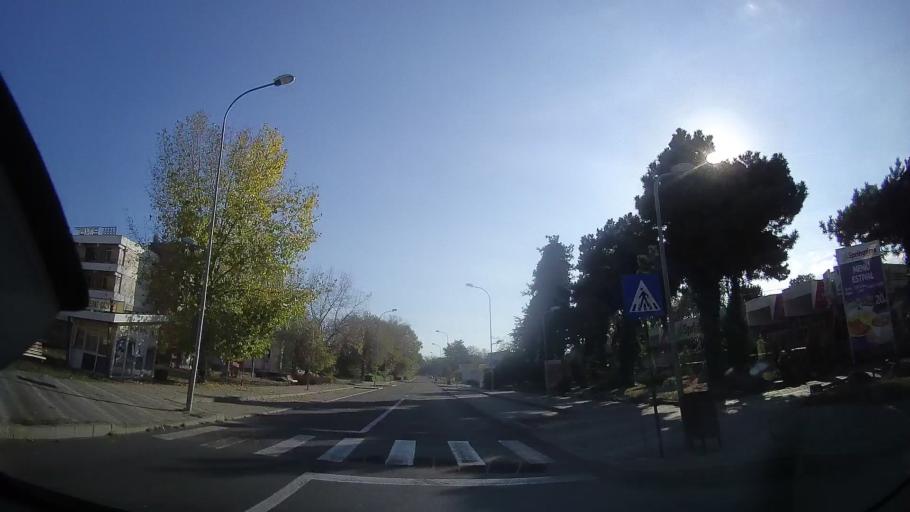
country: RO
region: Constanta
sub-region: Comuna Douazeci si Trei August
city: Douazeci si Trei August
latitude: 43.8641
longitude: 28.5977
